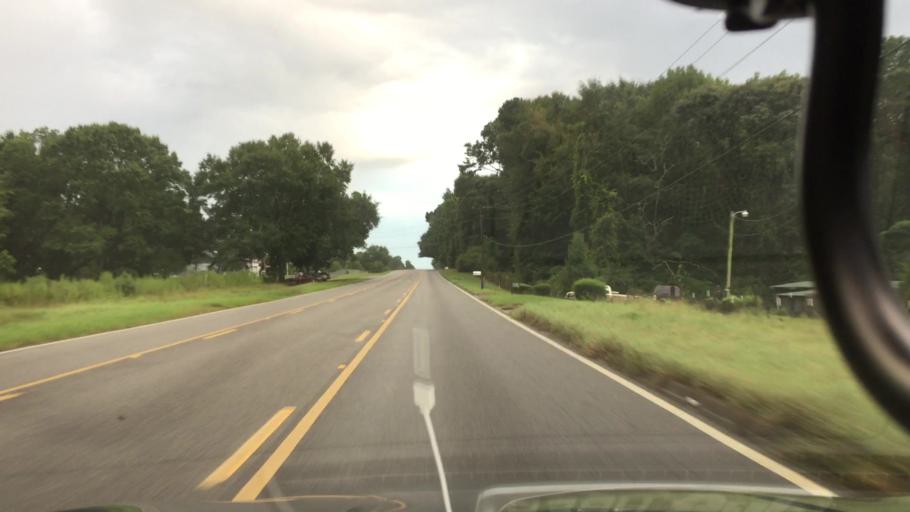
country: US
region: Alabama
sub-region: Pike County
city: Troy
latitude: 31.6858
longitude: -85.9595
